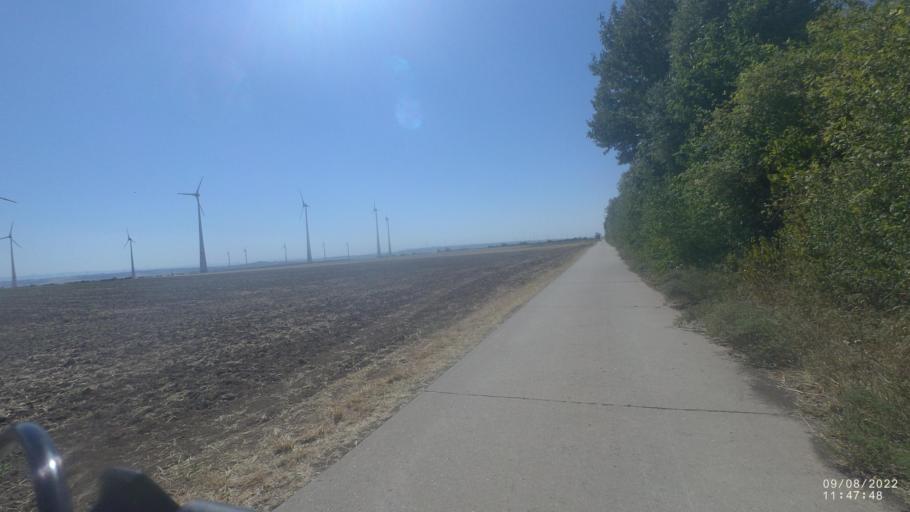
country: DE
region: Rheinland-Pfalz
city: Worrstadt
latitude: 49.8367
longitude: 8.1289
